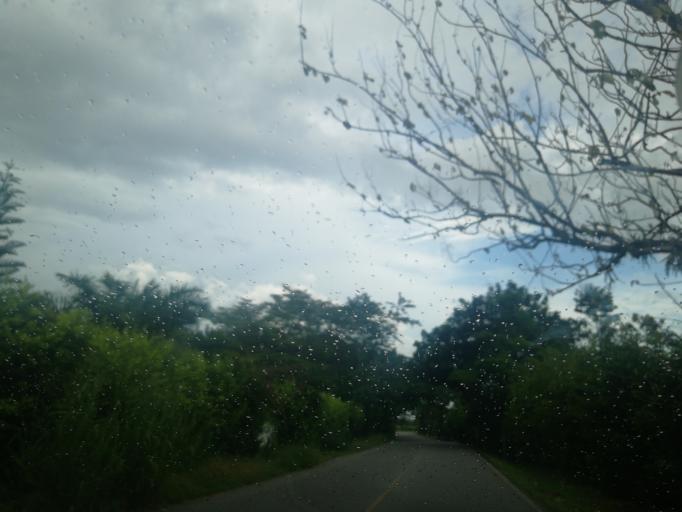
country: CO
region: Meta
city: Acacias
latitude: 3.9864
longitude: -73.7284
